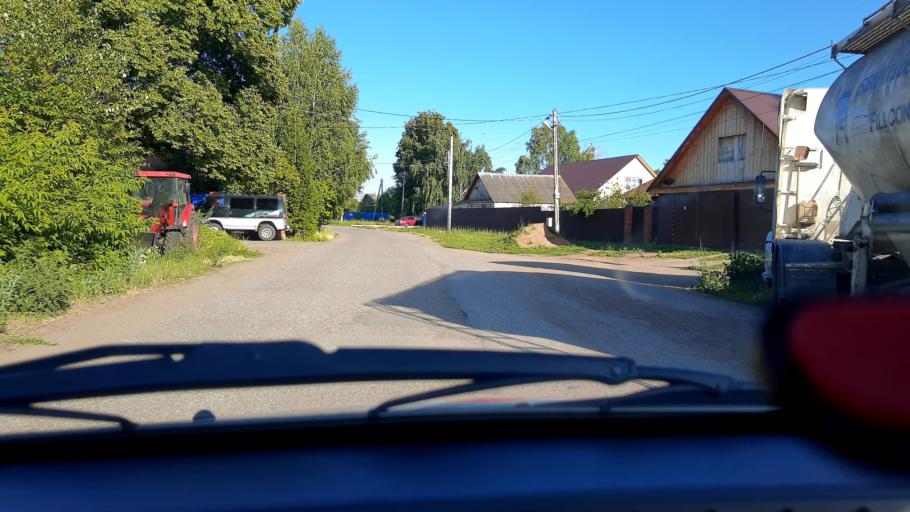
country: RU
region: Bashkortostan
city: Avdon
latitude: 54.4974
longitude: 55.8904
